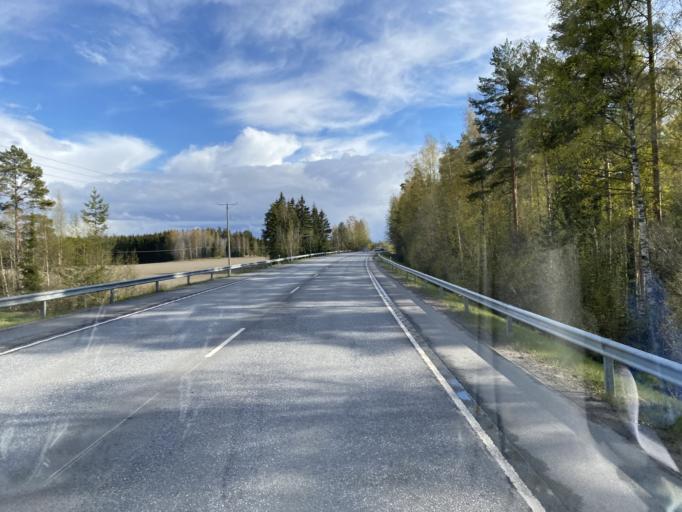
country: FI
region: Pirkanmaa
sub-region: Tampere
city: Lempaeaelae
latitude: 61.2740
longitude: 23.7476
